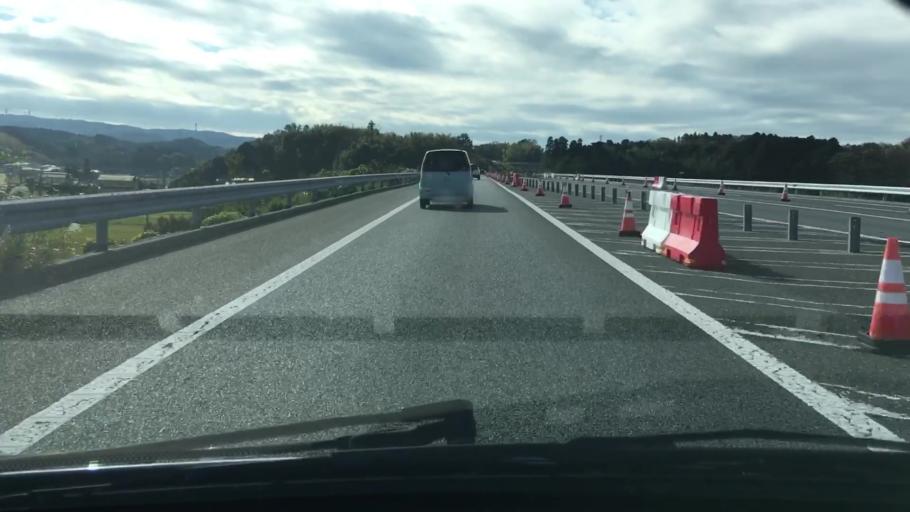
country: JP
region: Chiba
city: Kimitsu
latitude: 35.3072
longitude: 139.9421
